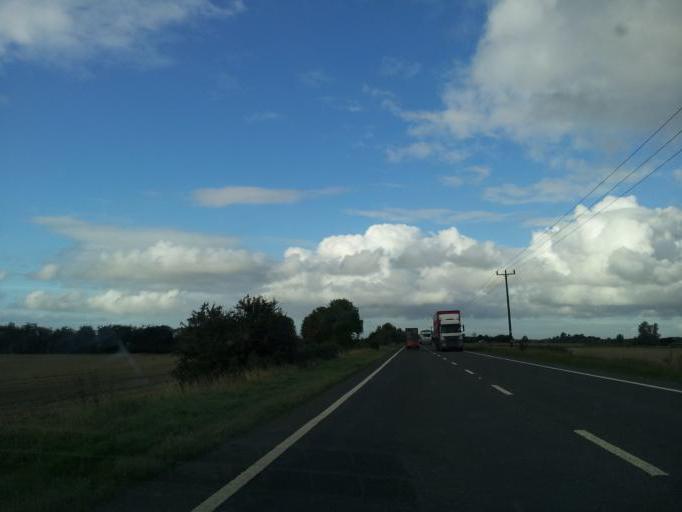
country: GB
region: England
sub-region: Norfolk
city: Clenchwarton
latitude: 52.7473
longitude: 0.3565
